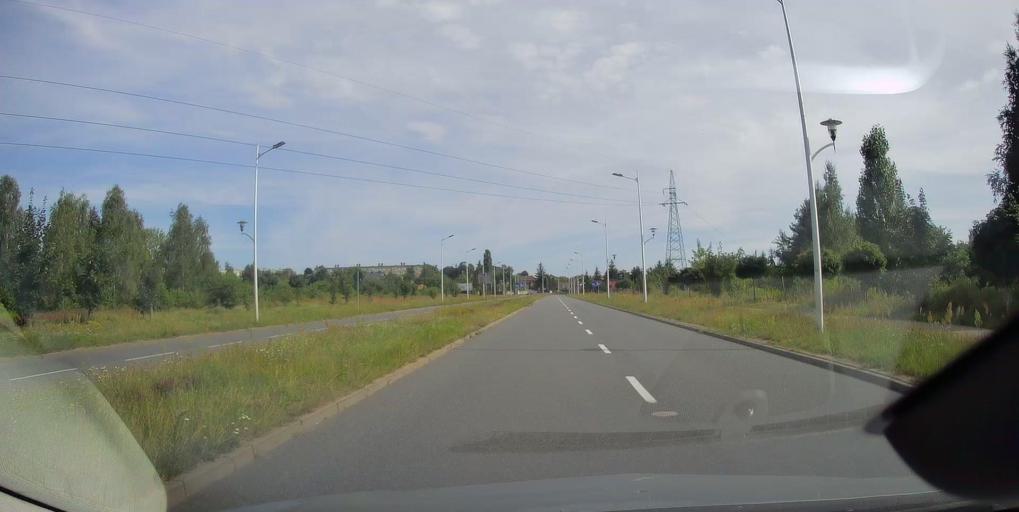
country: PL
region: Lodz Voivodeship
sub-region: Powiat tomaszowski
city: Tomaszow Mazowiecki
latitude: 51.5463
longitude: 19.9921
